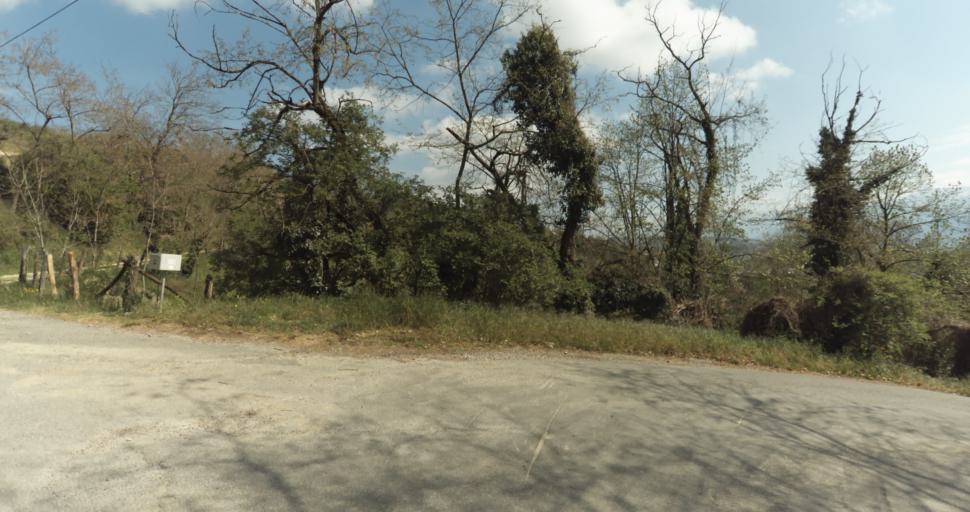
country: FR
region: Rhone-Alpes
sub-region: Departement de l'Isere
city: Saint-Marcellin
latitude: 45.1569
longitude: 5.3077
